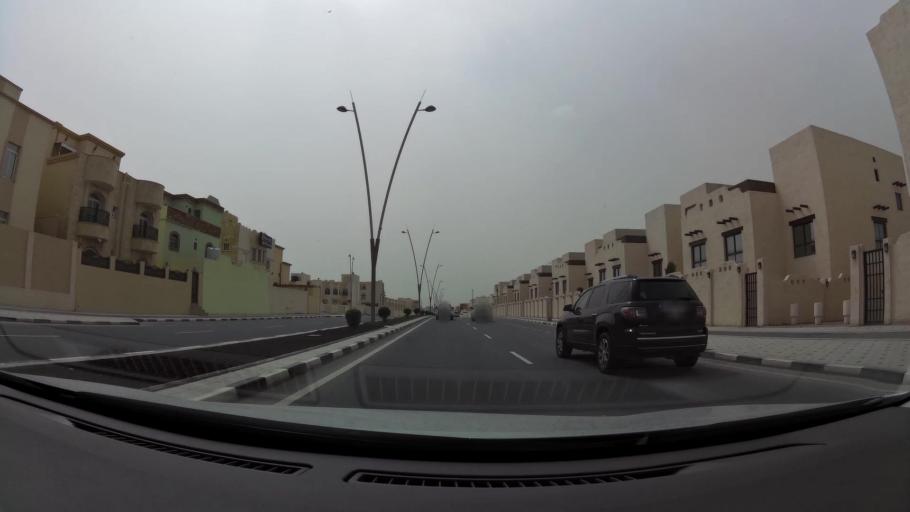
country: QA
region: Baladiyat ad Dawhah
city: Doha
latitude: 25.2327
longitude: 51.5485
